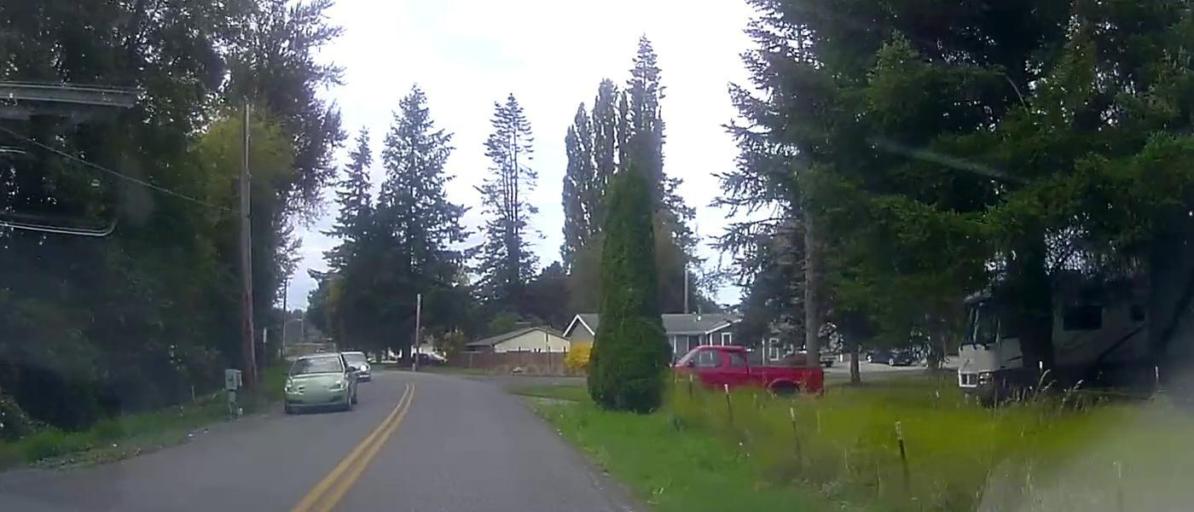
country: US
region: Washington
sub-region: Skagit County
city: Sedro-Woolley
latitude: 48.4985
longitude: -122.2500
